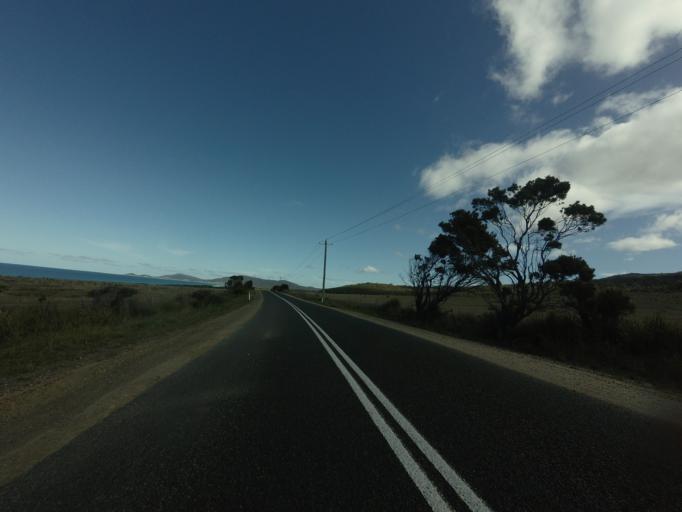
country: AU
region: Tasmania
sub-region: Break O'Day
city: St Helens
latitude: -41.7976
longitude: 148.2611
